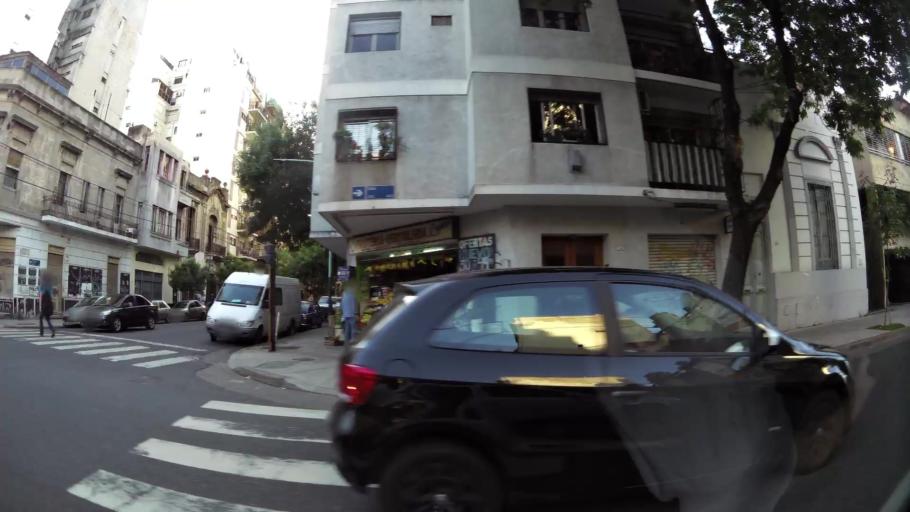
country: AR
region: Buenos Aires F.D.
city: Retiro
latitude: -34.6050
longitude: -58.4134
